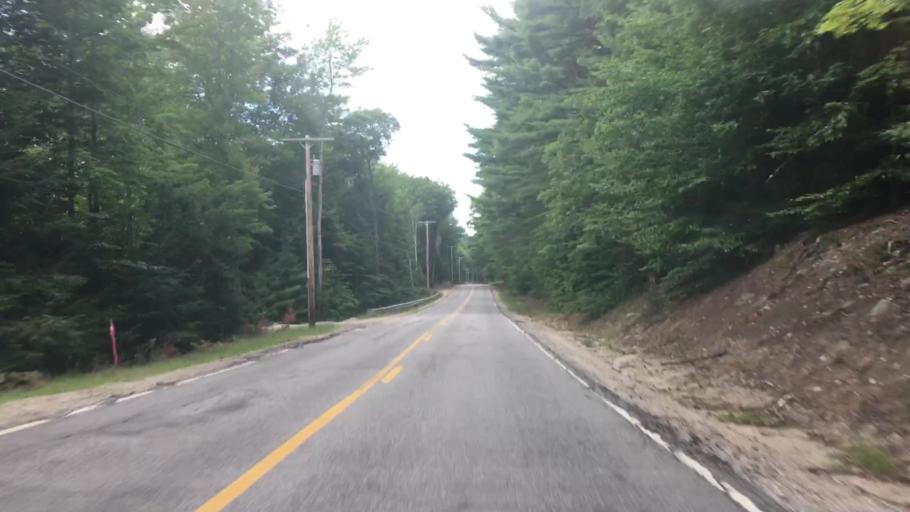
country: US
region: Maine
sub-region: Oxford County
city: Oxford
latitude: 44.0254
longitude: -70.5300
